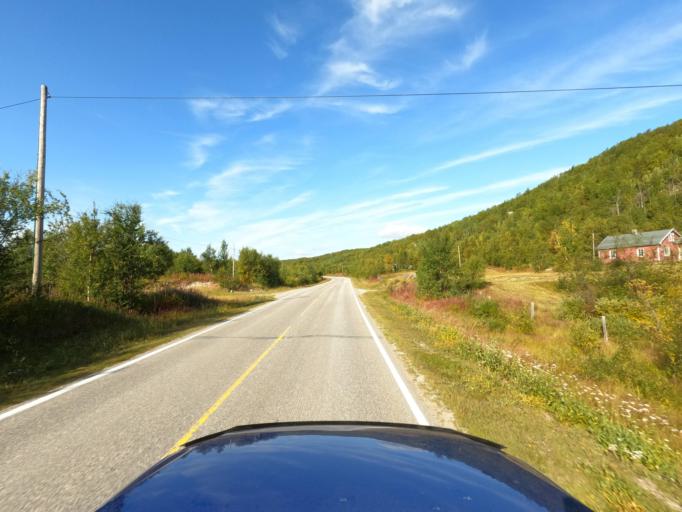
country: NO
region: Finnmark Fylke
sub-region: Porsanger
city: Lakselv
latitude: 69.7602
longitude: 25.2050
